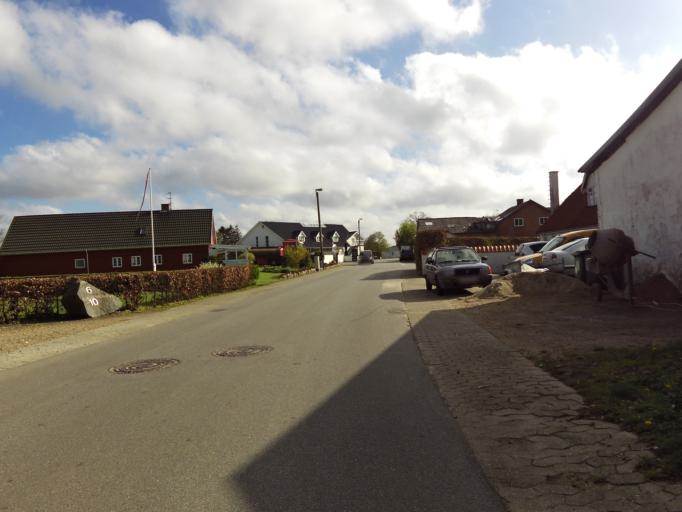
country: DK
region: South Denmark
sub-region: Haderslev Kommune
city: Gram
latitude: 55.3167
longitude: 8.9833
